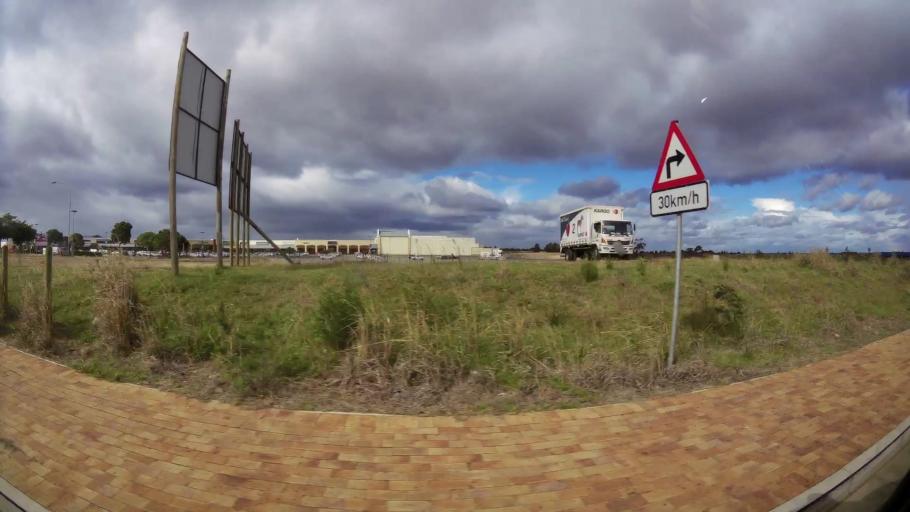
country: ZA
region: Western Cape
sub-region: Eden District Municipality
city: George
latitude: -33.9867
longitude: 22.4995
